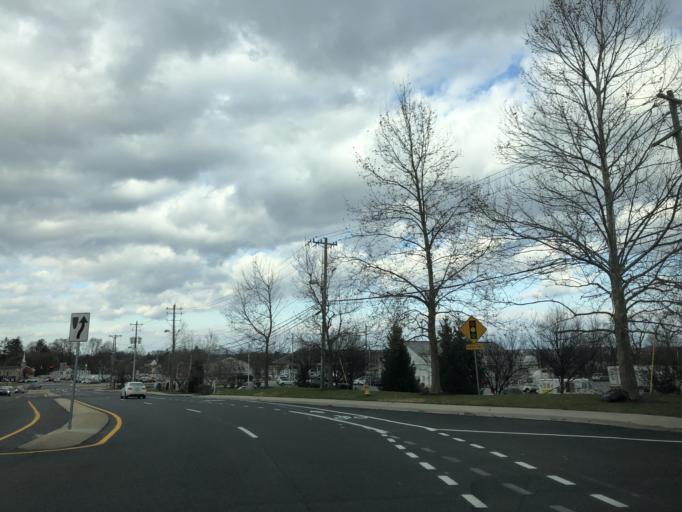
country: US
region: Delaware
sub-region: New Castle County
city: Wilmington Manor
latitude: 39.7085
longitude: -75.5618
